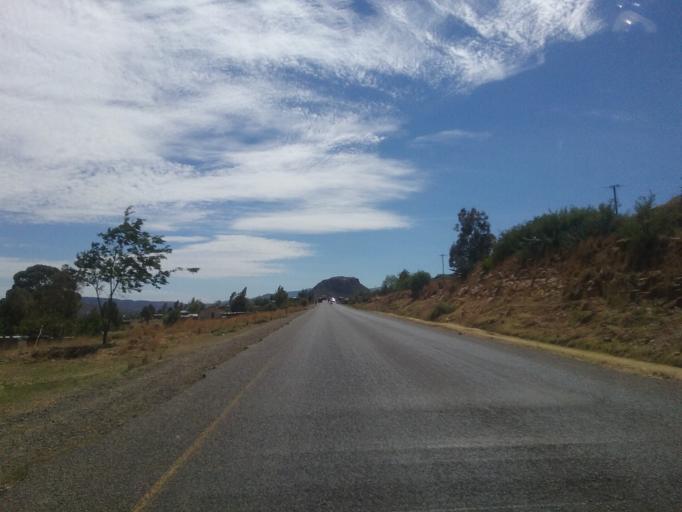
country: LS
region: Mohale's Hoek District
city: Mohale's Hoek
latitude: -30.1836
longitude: 27.4246
